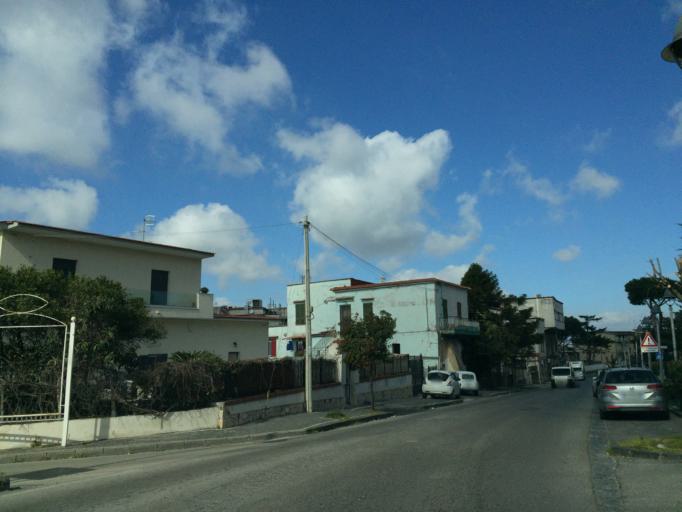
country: IT
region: Campania
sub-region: Provincia di Napoli
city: Pollena Trocchia
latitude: 40.8509
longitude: 14.3749
